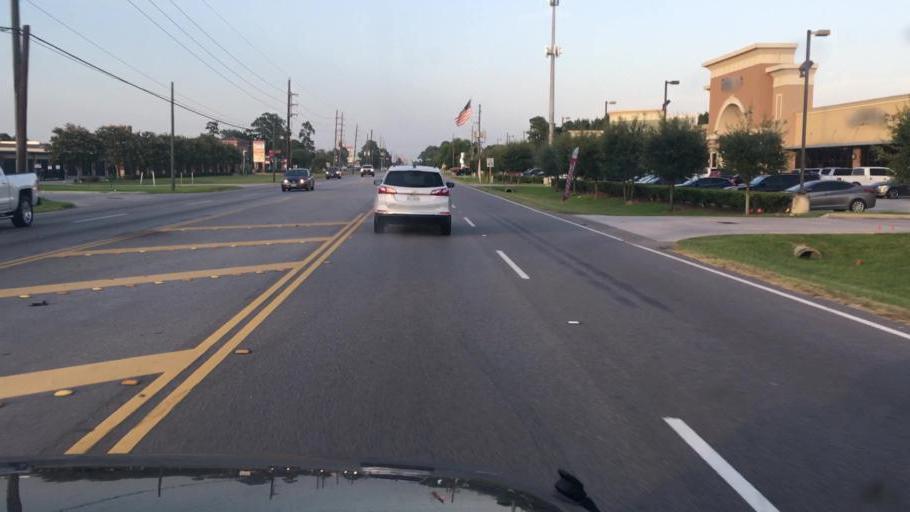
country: US
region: Texas
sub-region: Harris County
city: Atascocita
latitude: 29.9933
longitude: -95.1779
